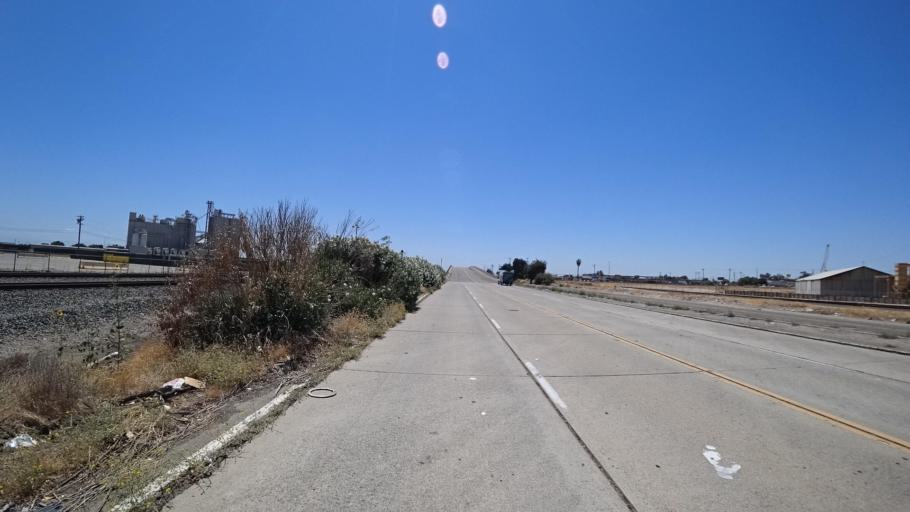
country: US
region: California
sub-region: Fresno County
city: Fresno
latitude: 36.6949
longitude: -119.7527
